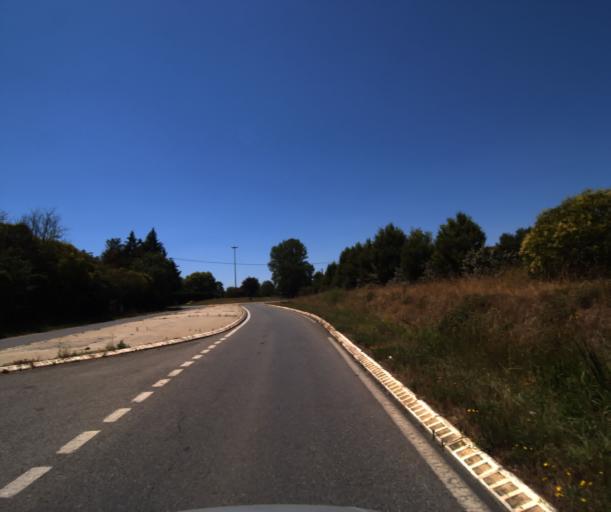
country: FR
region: Midi-Pyrenees
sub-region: Departement de la Haute-Garonne
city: Seysses
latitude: 43.4641
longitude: 1.3004
